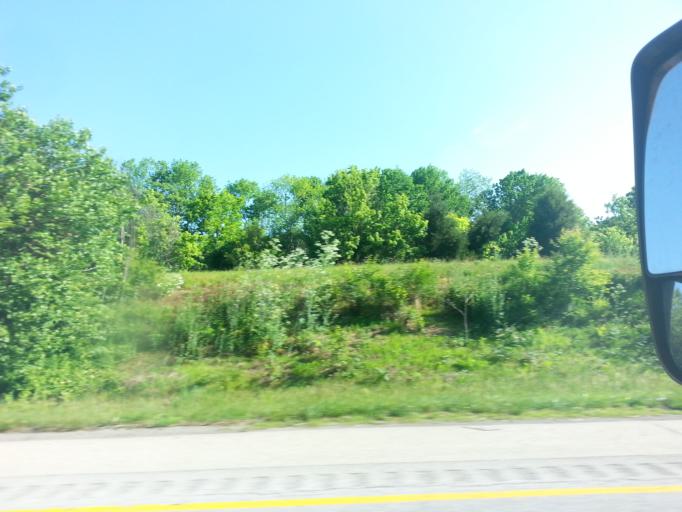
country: US
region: Kentucky
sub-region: Jefferson County
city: Middletown
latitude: 38.2228
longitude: -85.5199
